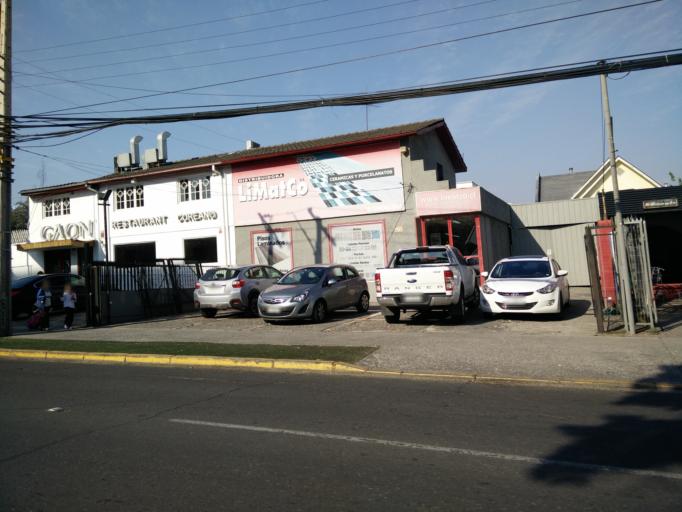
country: CL
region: Santiago Metropolitan
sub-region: Provincia de Santiago
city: Villa Presidente Frei, Nunoa, Santiago, Chile
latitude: -33.4131
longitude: -70.5658
